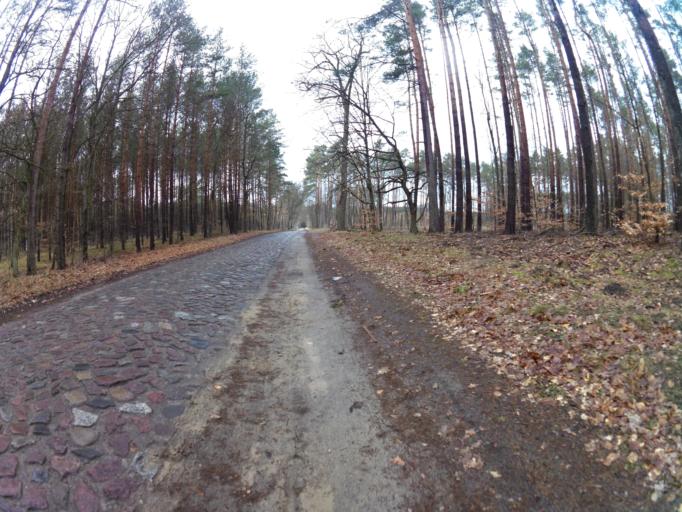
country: PL
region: West Pomeranian Voivodeship
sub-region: Powiat mysliborski
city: Debno
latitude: 52.7282
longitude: 14.7276
